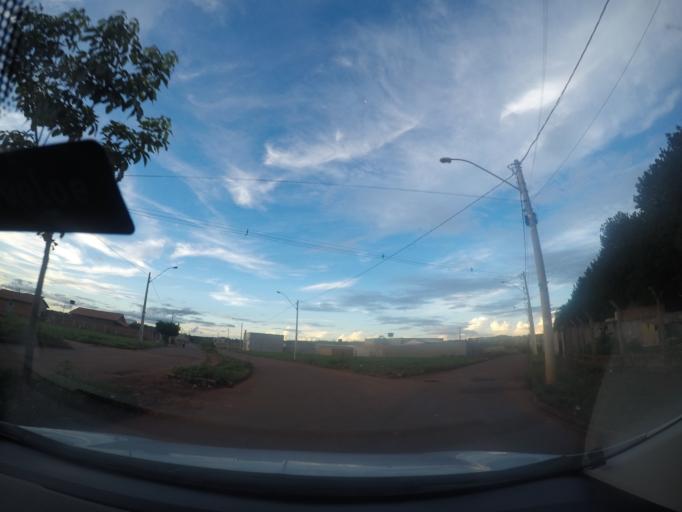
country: BR
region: Goias
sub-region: Goianira
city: Goianira
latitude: -16.5685
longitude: -49.3744
